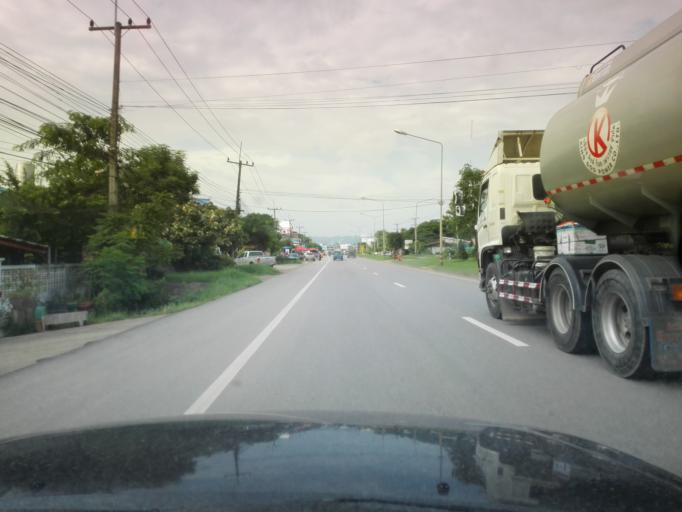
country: TH
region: Tak
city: Mae Sot
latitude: 16.7172
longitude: 98.5593
